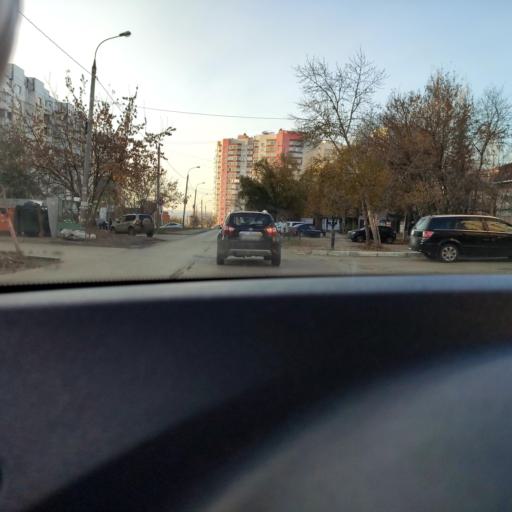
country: RU
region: Samara
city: Samara
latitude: 53.2528
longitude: 50.2055
